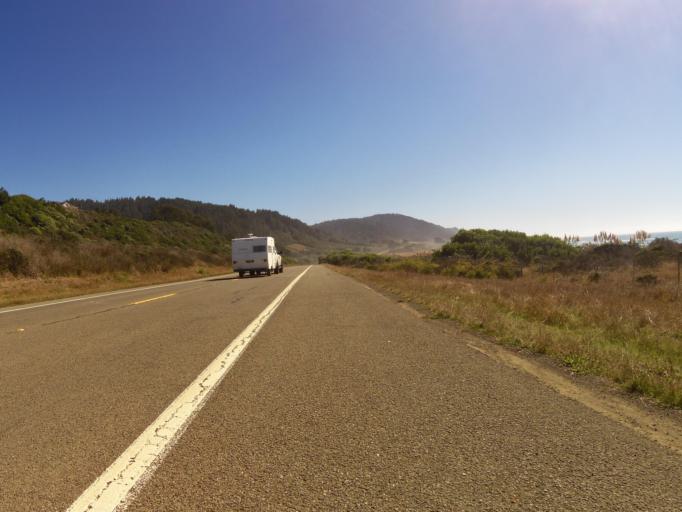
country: US
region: California
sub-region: Mendocino County
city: Fort Bragg
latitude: 39.6647
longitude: -123.7878
